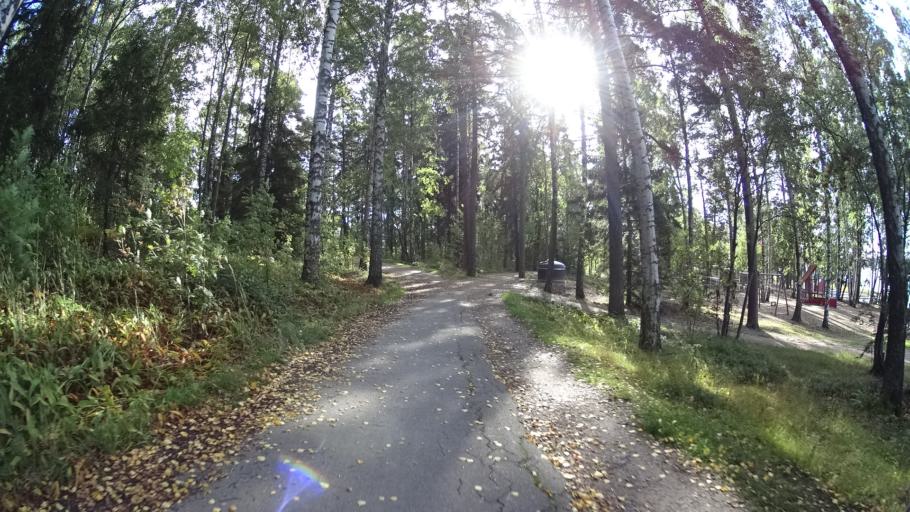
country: FI
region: Uusimaa
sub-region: Helsinki
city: Teekkarikylae
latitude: 60.2012
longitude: 24.8575
